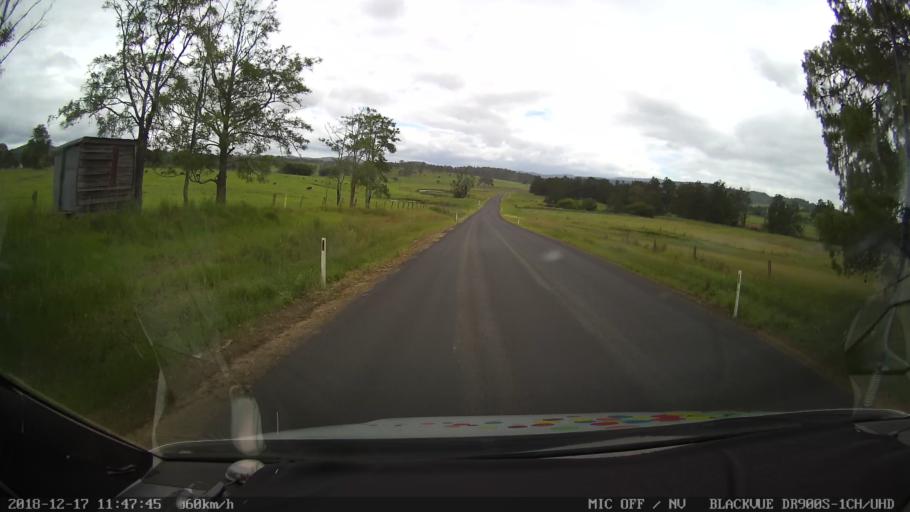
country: AU
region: New South Wales
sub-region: Kyogle
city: Kyogle
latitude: -28.6243
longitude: 152.5909
